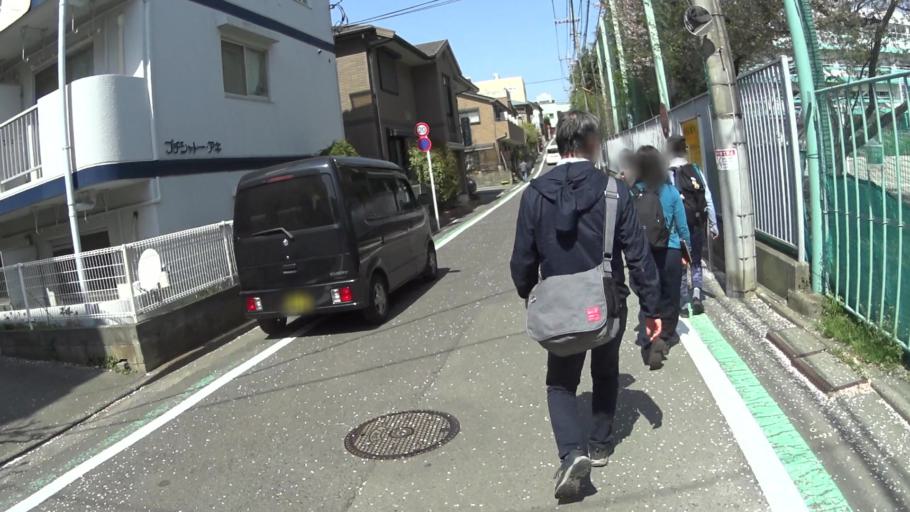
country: JP
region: Tokyo
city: Kokubunji
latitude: 35.7053
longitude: 139.4823
